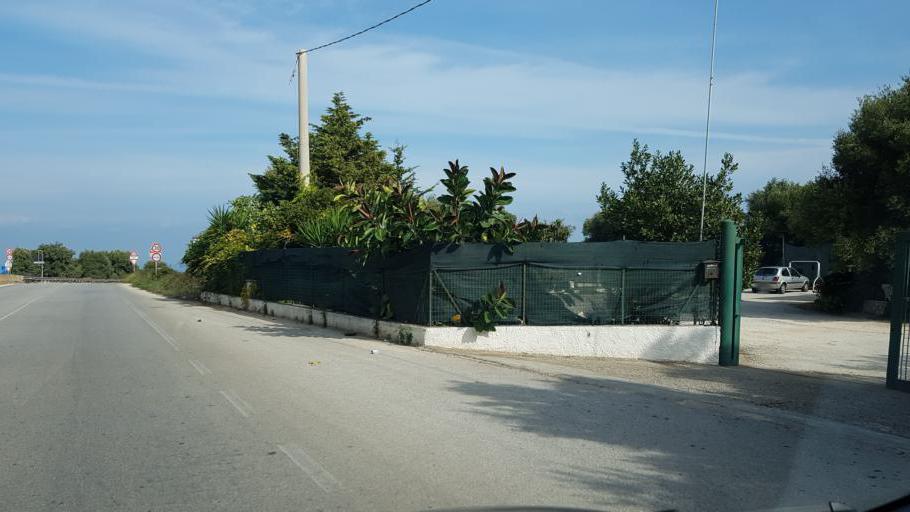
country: IT
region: Apulia
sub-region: Provincia di Brindisi
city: Ostuni
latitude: 40.7551
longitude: 17.5832
